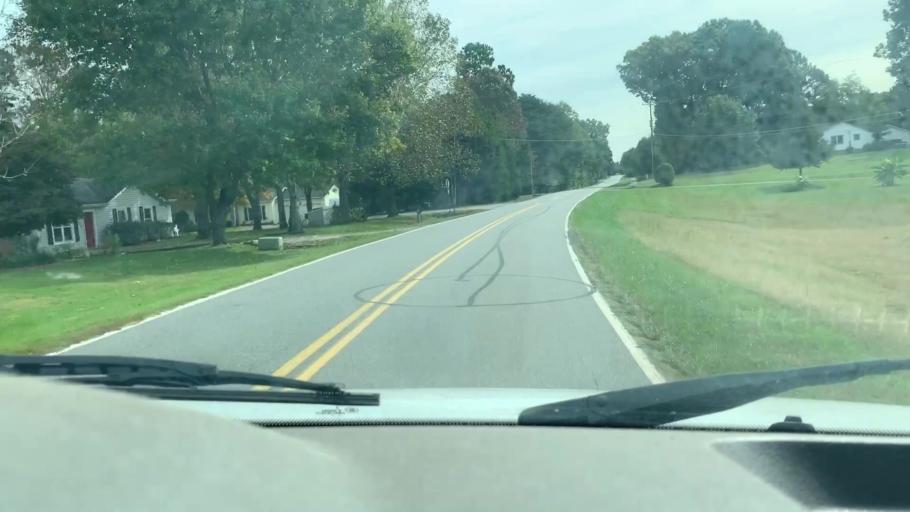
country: US
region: North Carolina
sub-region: Catawba County
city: Lake Norman of Catawba
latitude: 35.5652
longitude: -80.9275
